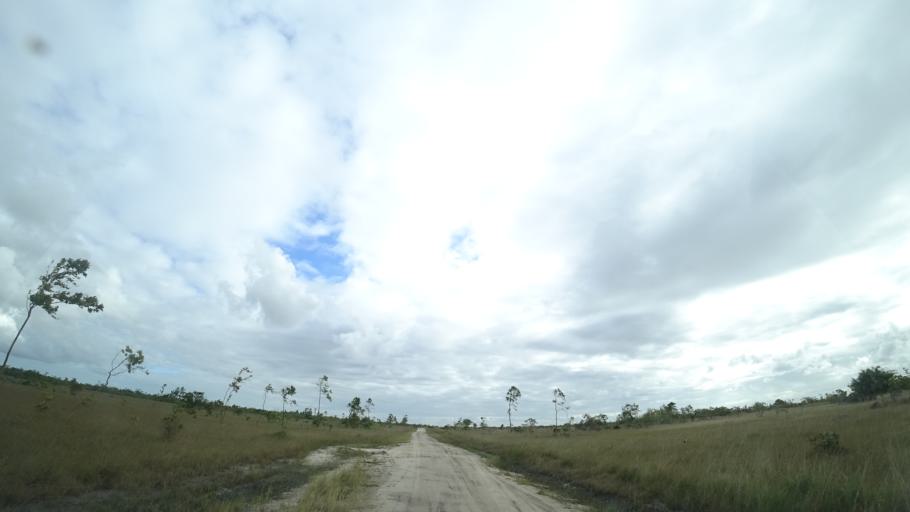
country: MZ
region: Sofala
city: Beira
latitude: -19.6129
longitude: 35.0712
